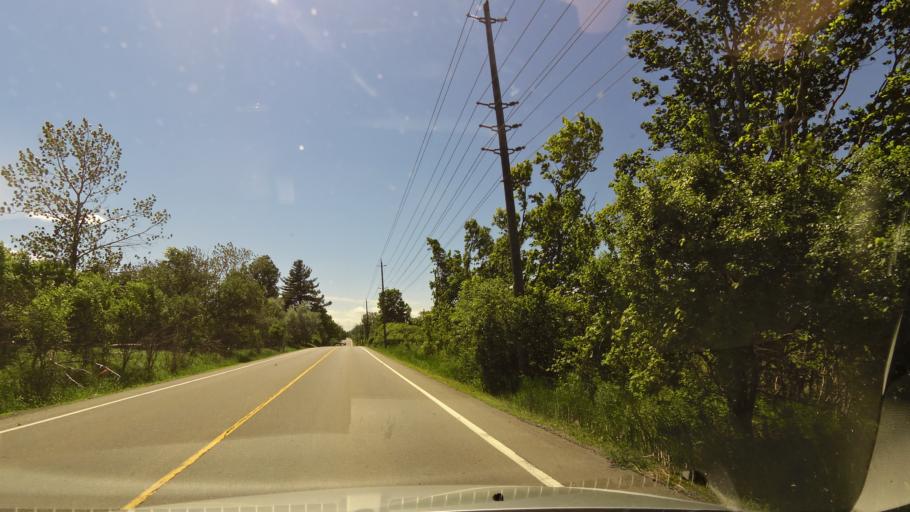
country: CA
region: Ontario
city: Newmarket
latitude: 43.9516
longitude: -79.5121
